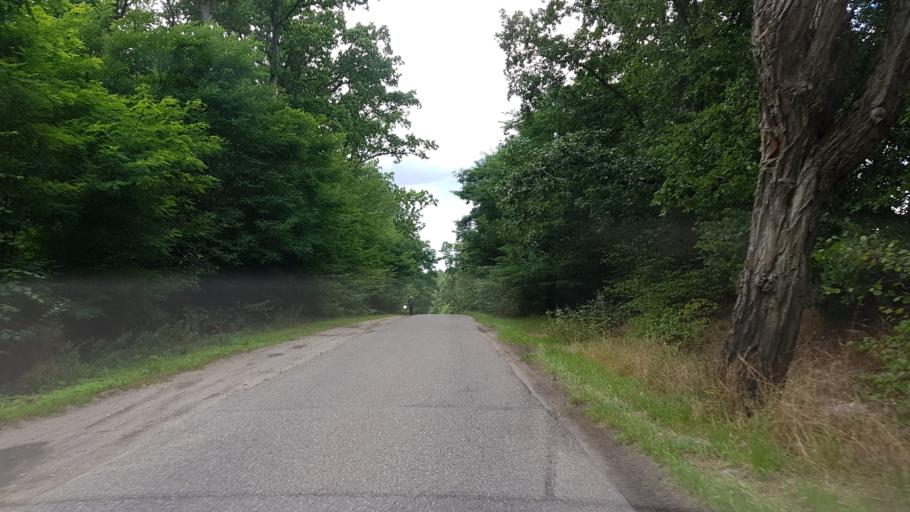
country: PL
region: West Pomeranian Voivodeship
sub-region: Powiat bialogardzki
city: Tychowo
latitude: 54.0270
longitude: 16.3553
